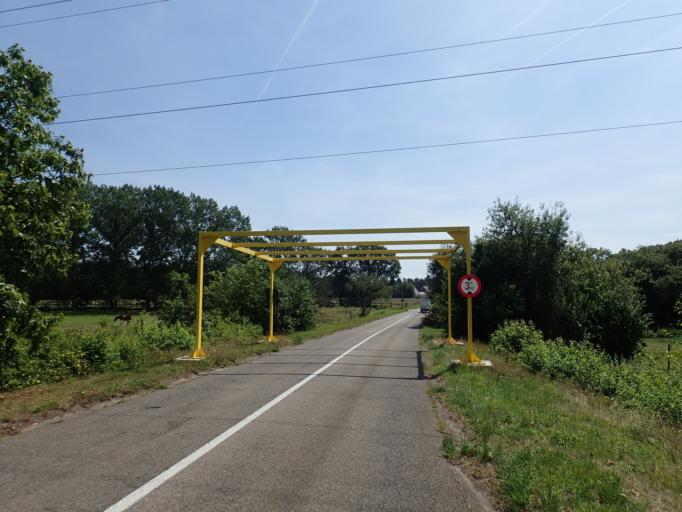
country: BE
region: Flanders
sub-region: Provincie Antwerpen
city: Zandhoven
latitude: 51.2216
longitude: 4.6484
